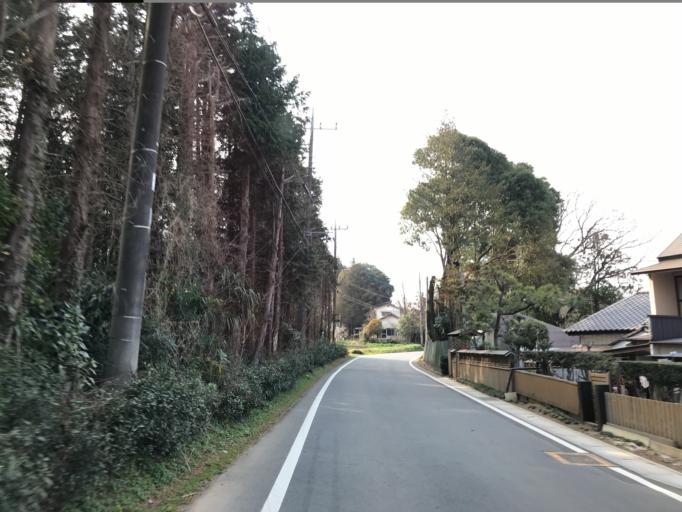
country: JP
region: Ibaraki
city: Okunoya
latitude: 36.2269
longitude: 140.4027
